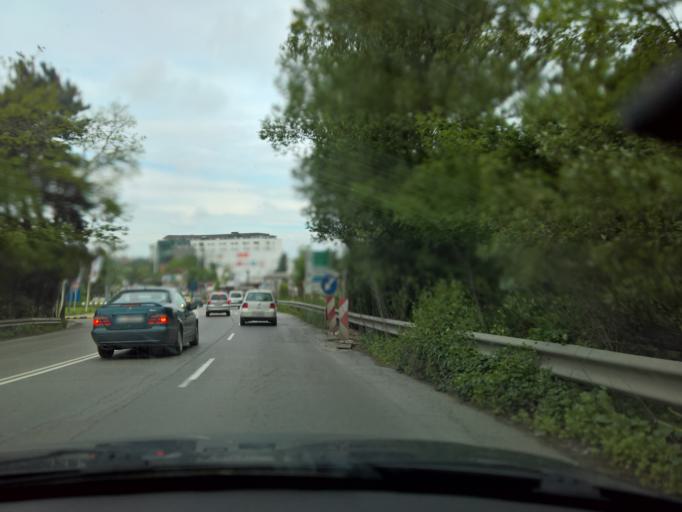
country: BG
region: Sofia-Capital
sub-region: Stolichna Obshtina
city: Sofia
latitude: 42.6641
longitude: 23.2612
